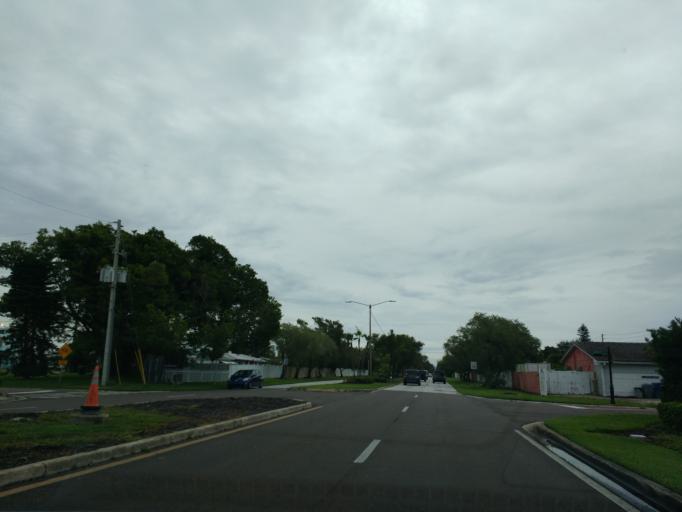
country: US
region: Florida
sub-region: Pinellas County
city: Treasure Island
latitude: 27.7707
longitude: -82.7506
